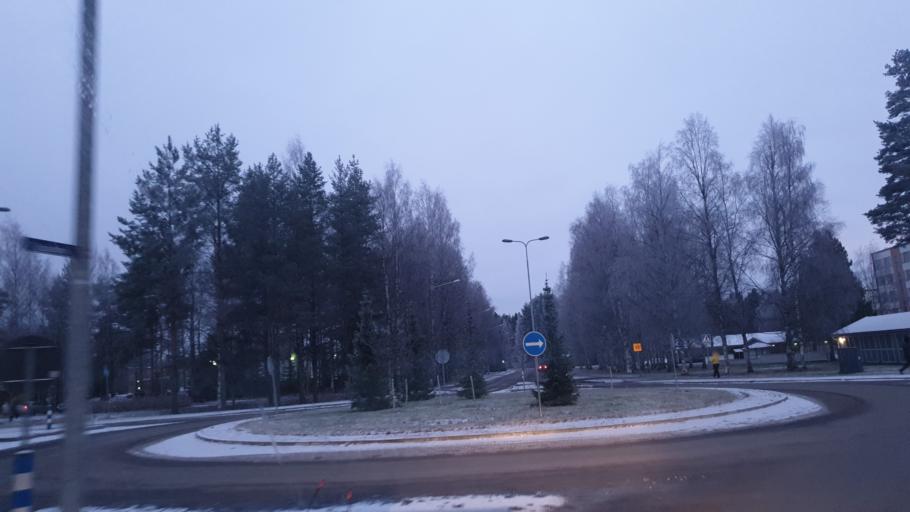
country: FI
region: Southern Ostrobothnia
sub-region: Seinaejoki
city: Seinaejoki
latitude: 62.7718
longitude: 22.8763
